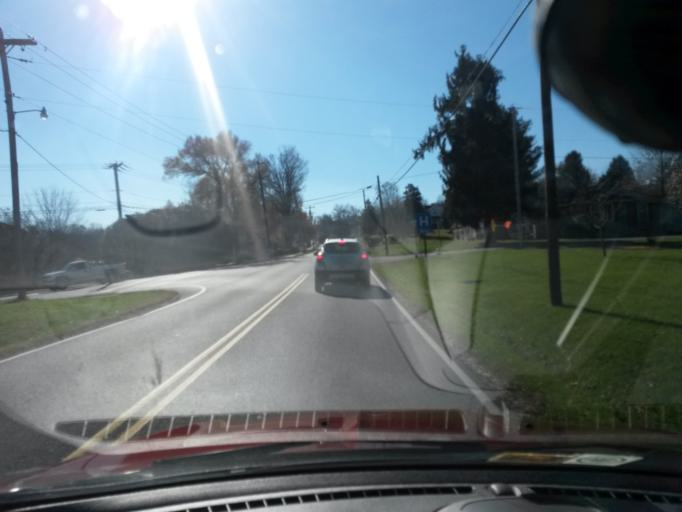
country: US
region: Virginia
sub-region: City of Bedford
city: Bedford
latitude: 37.3498
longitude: -79.5271
